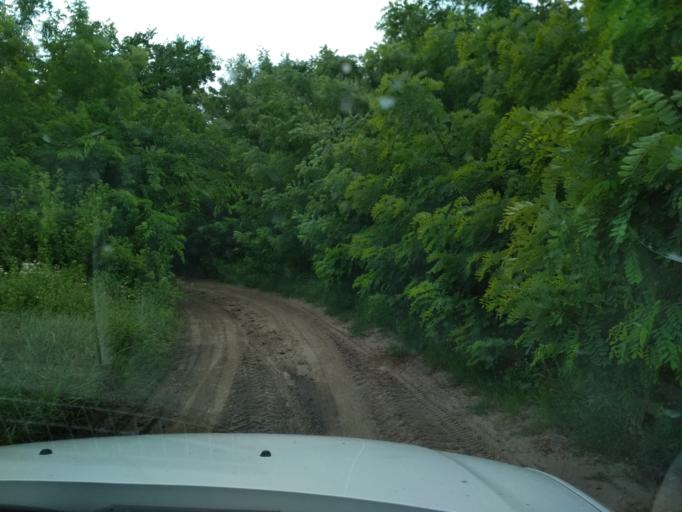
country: HU
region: Pest
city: Tapioszentmarton
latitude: 47.3669
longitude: 19.7464
